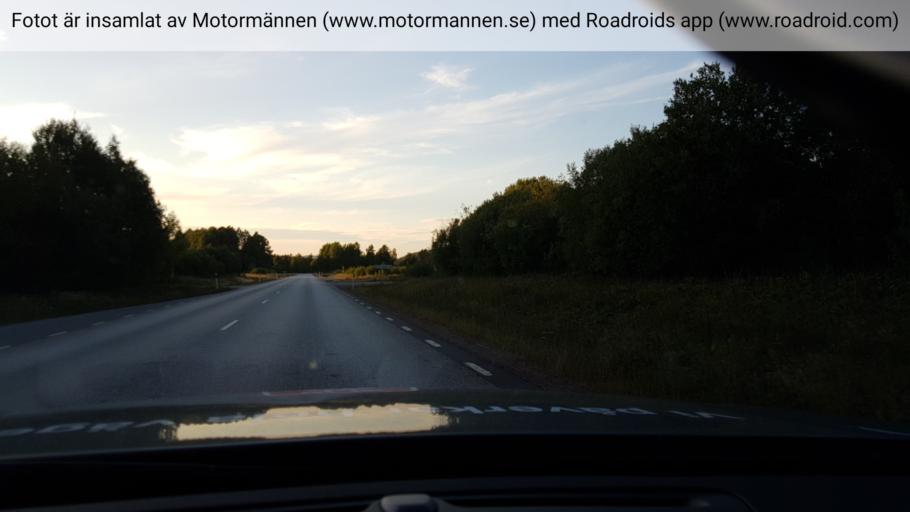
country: SE
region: Vaermland
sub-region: Storfors Kommun
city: Storfors
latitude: 59.5290
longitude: 14.2965
